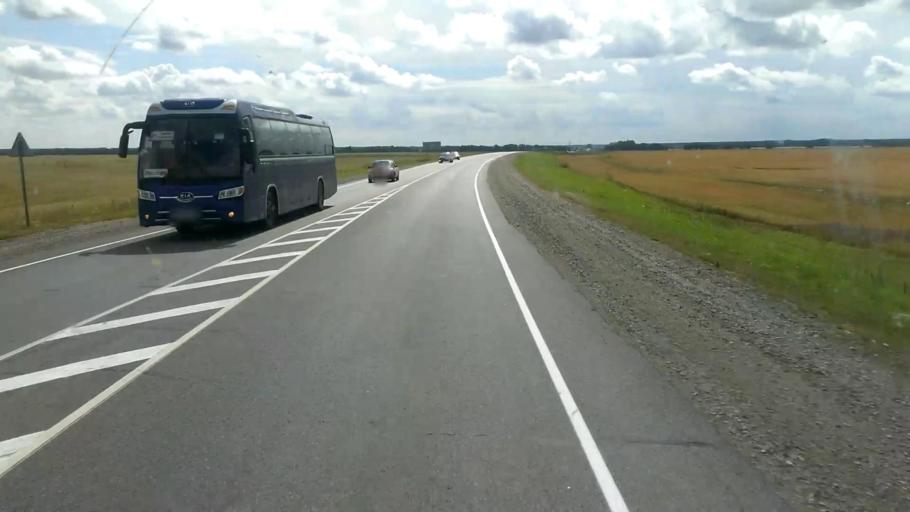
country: RU
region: Altai Krai
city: Troitskoye
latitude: 52.9057
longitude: 84.8296
